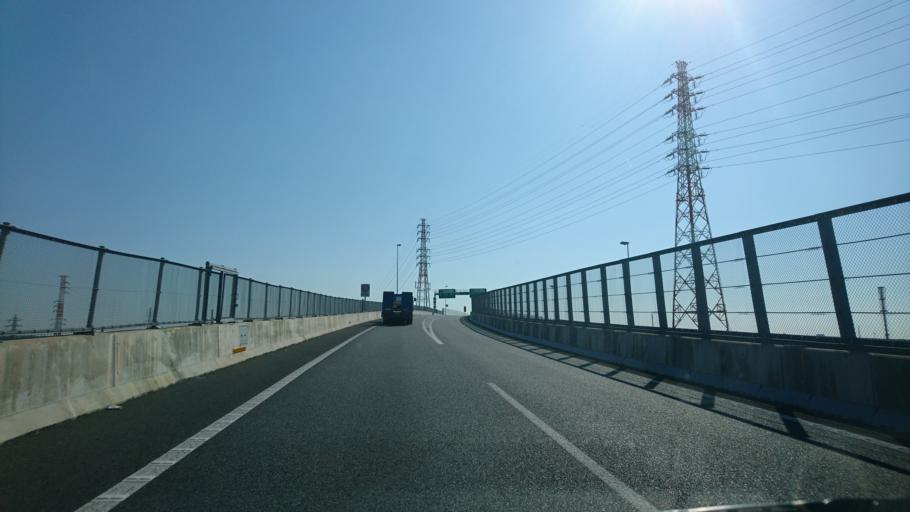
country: JP
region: Kanagawa
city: Chigasaki
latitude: 35.3512
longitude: 139.3900
